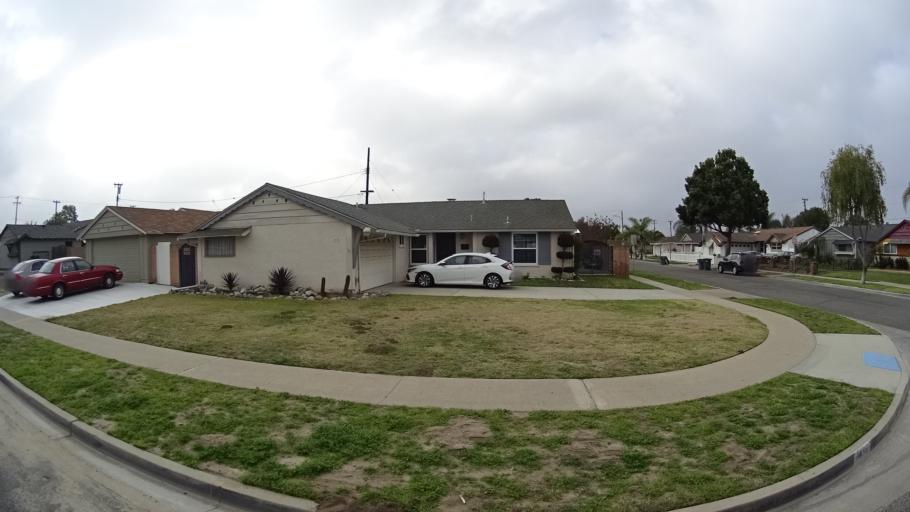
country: US
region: California
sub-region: Orange County
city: Buena Park
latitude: 33.8371
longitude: -118.0034
